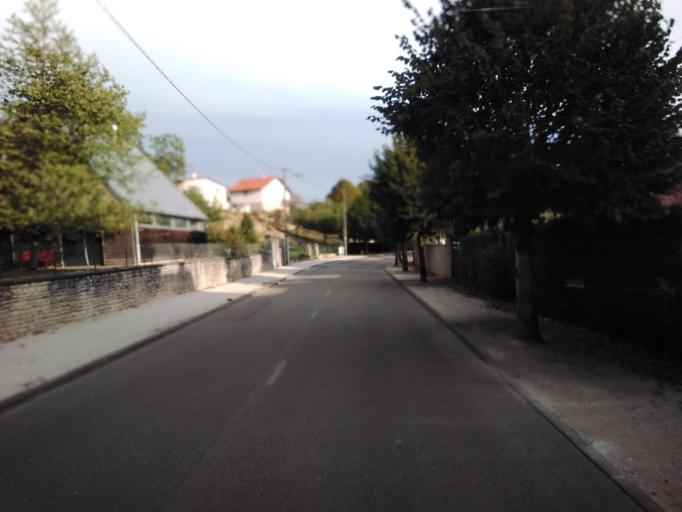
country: FR
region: Champagne-Ardenne
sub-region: Departement de l'Aube
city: Les Riceys
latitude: 47.8481
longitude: 4.3640
